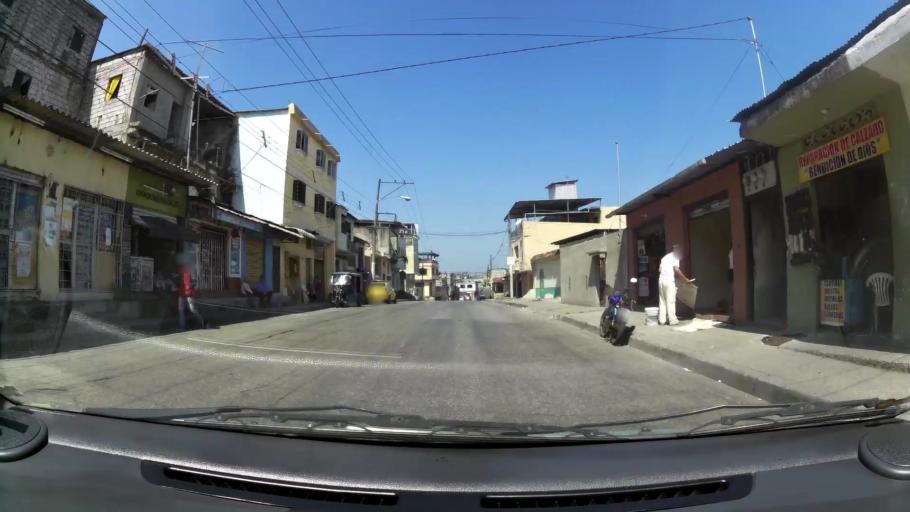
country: EC
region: Guayas
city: Guayaquil
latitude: -2.1295
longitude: -79.9194
